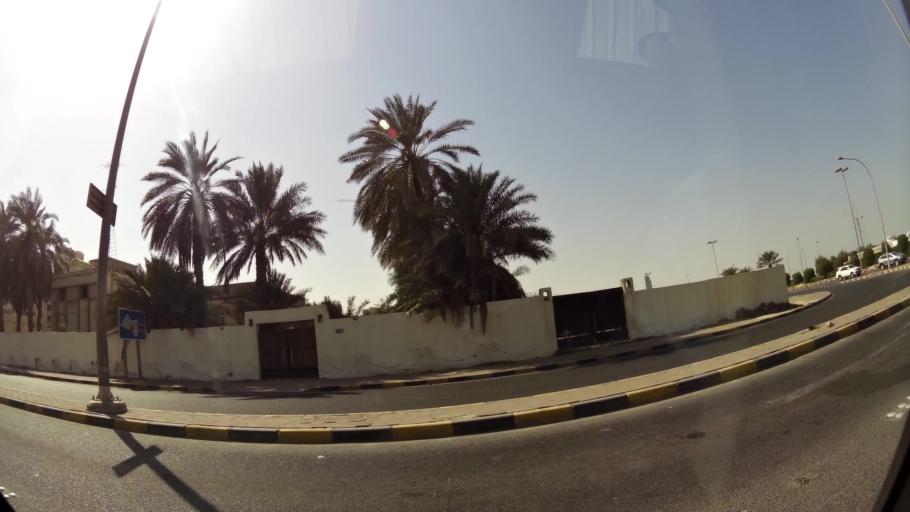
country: KW
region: Muhafazat Hawalli
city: As Salimiyah
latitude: 29.3398
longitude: 48.0625
